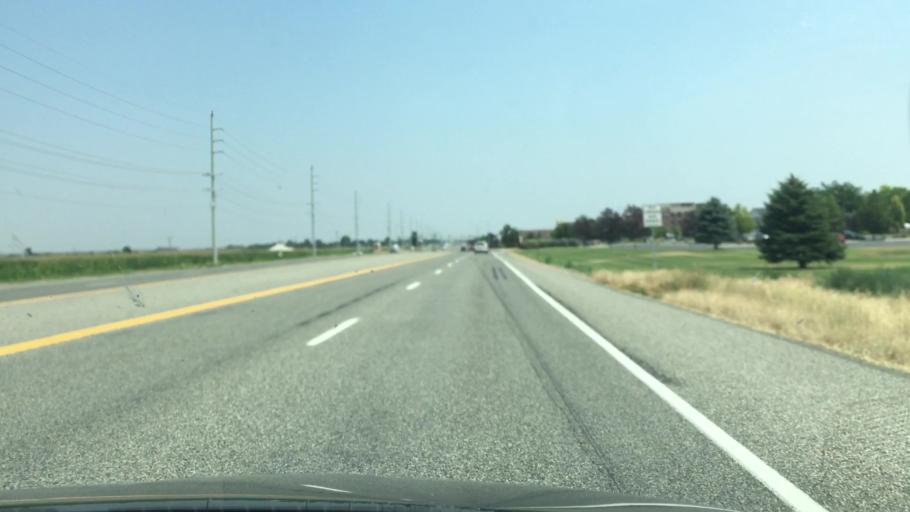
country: US
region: Idaho
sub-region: Twin Falls County
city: Twin Falls
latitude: 42.5916
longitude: -114.5046
